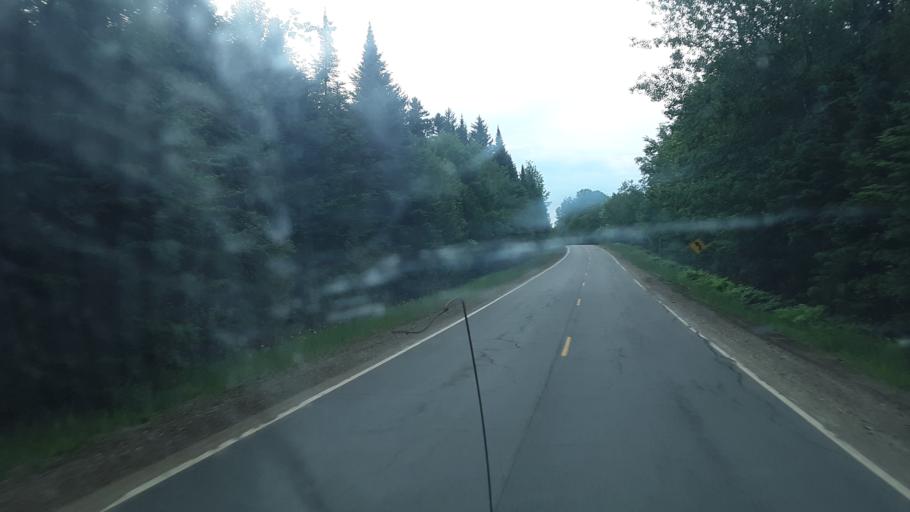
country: US
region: Maine
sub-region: Penobscot County
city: Medway
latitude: 45.6742
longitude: -68.2800
